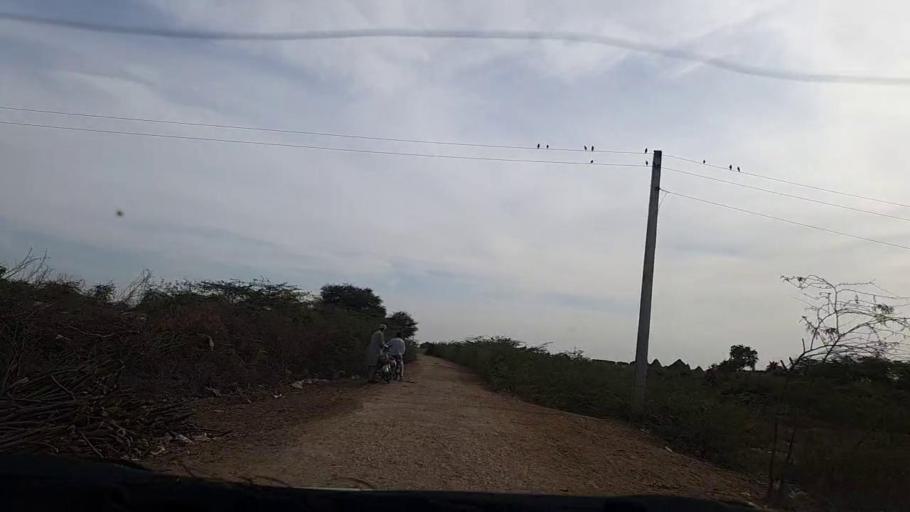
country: PK
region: Sindh
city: Dhoro Naro
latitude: 25.4121
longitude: 69.5184
